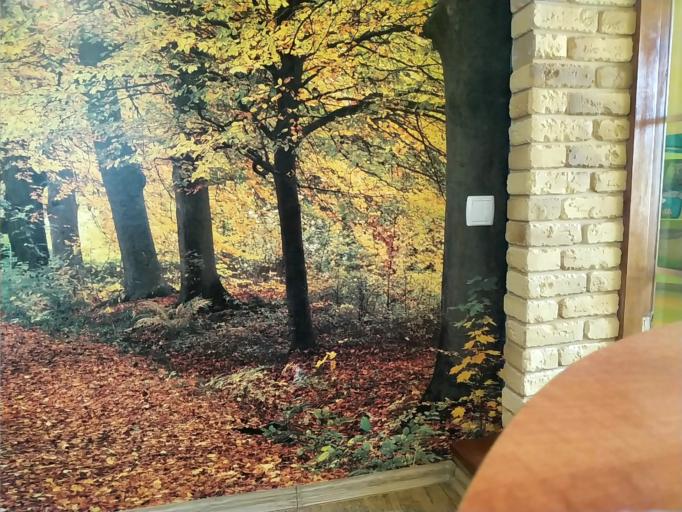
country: RU
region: Arkhangelskaya
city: Onega
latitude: 63.7217
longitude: 38.0843
